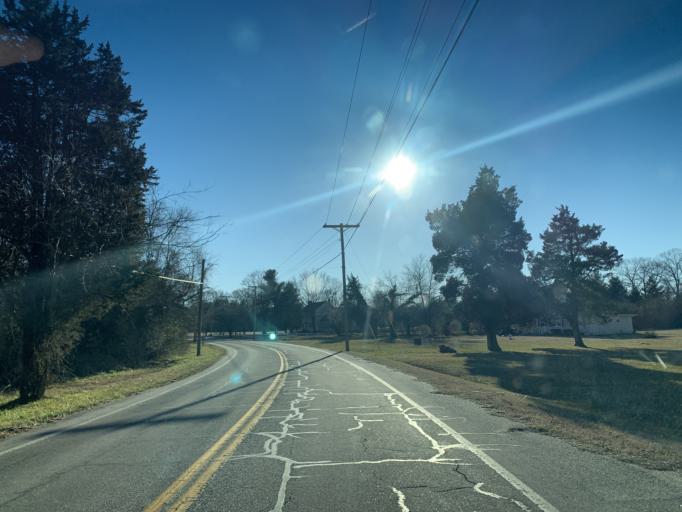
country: US
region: Maryland
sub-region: Saint Mary's County
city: Charlotte Hall
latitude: 38.4873
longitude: -76.7788
